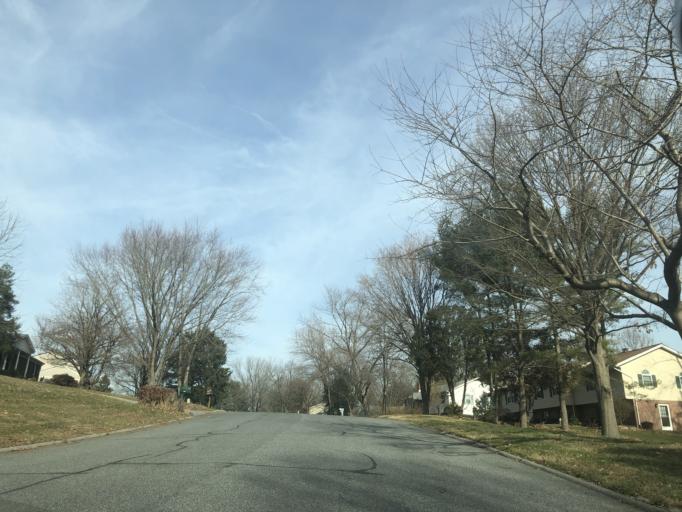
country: US
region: Maryland
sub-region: Howard County
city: Columbia
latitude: 39.2868
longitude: -76.8468
